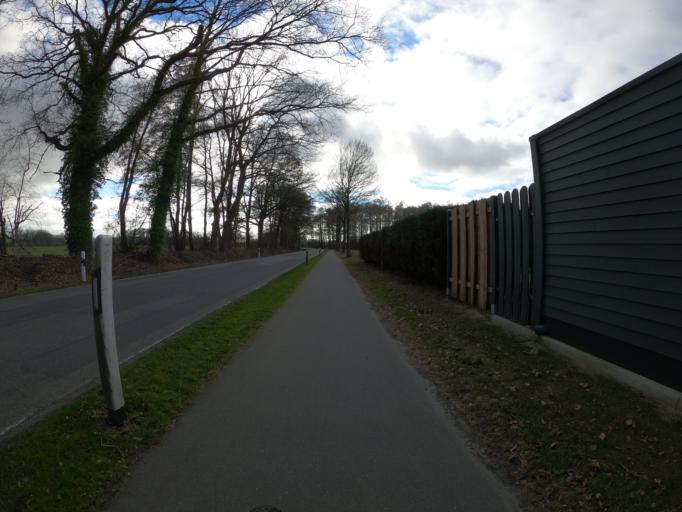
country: DE
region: Lower Saxony
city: Dohren
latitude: 52.6742
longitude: 7.5804
